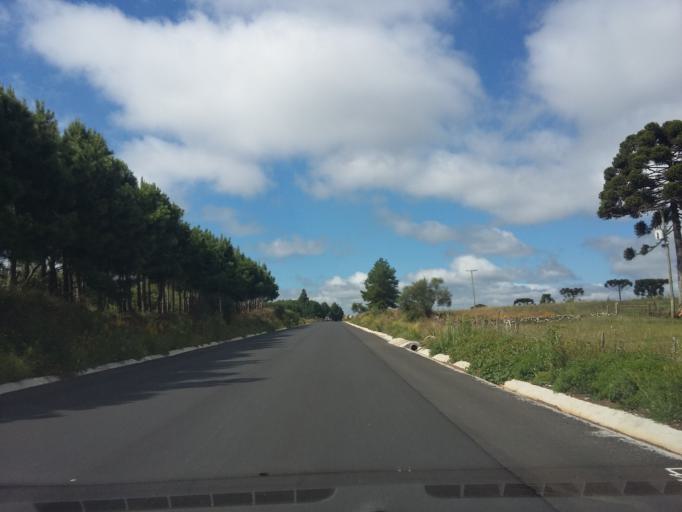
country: BR
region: Santa Catarina
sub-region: Sao Joaquim
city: Sao Joaquim
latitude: -28.0383
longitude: -50.0740
